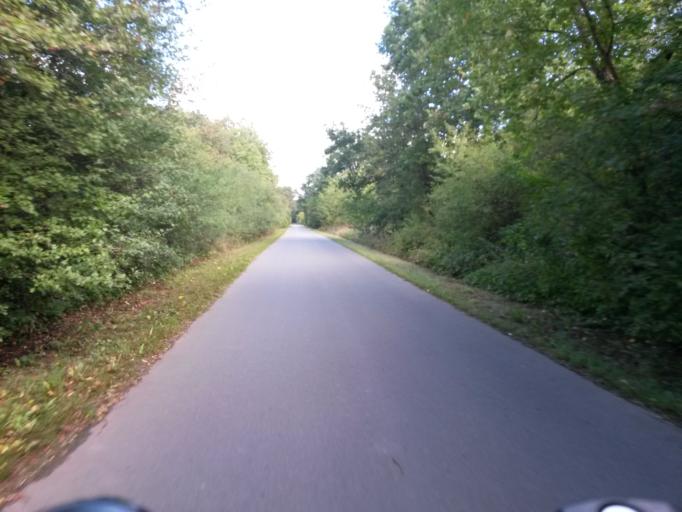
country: DE
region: Brandenburg
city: Templin
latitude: 53.2030
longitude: 13.5157
